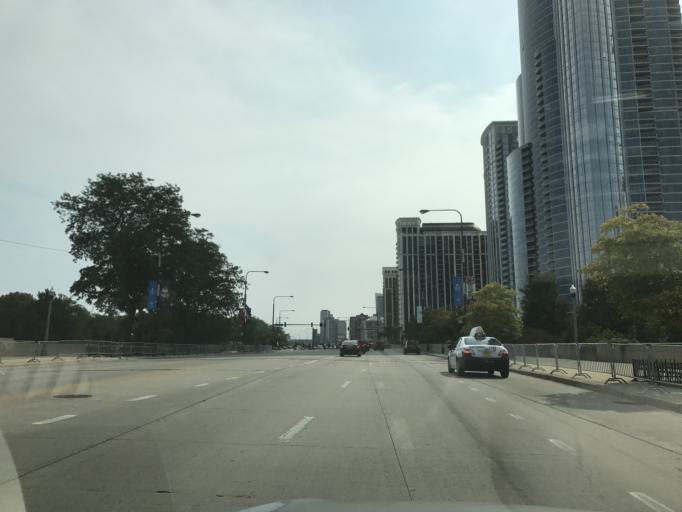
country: US
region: Illinois
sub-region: Cook County
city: Chicago
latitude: 41.8689
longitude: -87.6206
